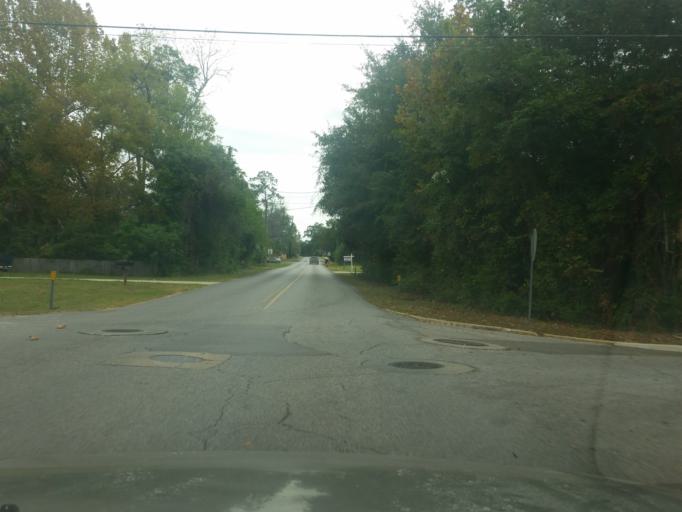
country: US
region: Florida
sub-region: Santa Rosa County
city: Milton
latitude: 30.6269
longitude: -87.0375
